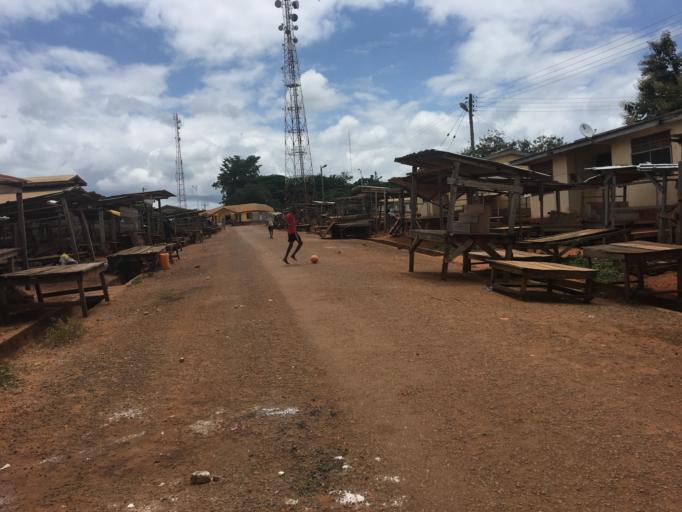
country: GH
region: Western
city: Bibiani
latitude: 6.8066
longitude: -2.5170
